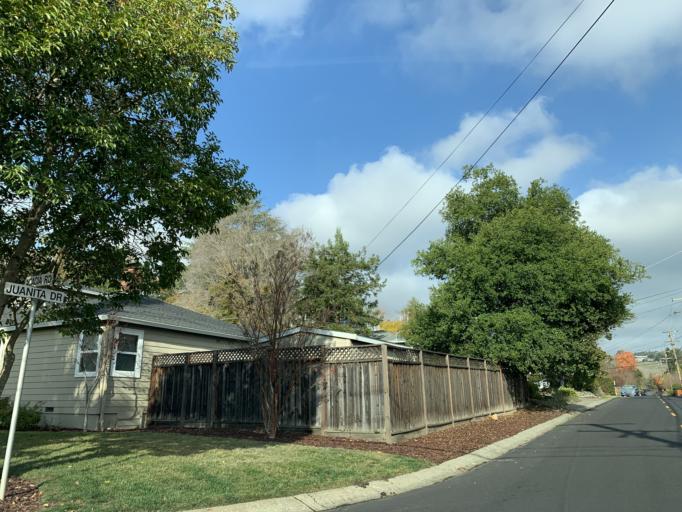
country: US
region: California
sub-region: Contra Costa County
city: Saranap
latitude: 37.8894
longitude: -122.0812
